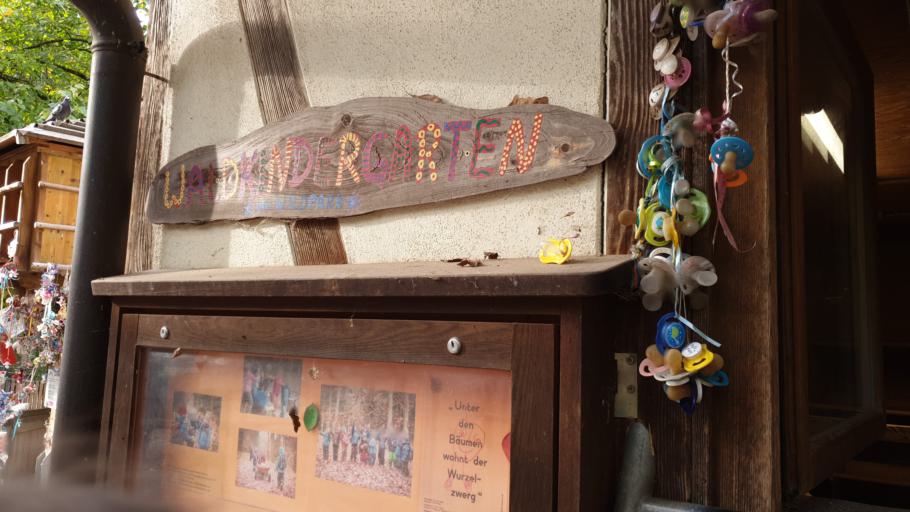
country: DE
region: Baden-Wuerttemberg
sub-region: Karlsruhe Region
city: Pforzheim
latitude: 48.8765
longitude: 8.7133
